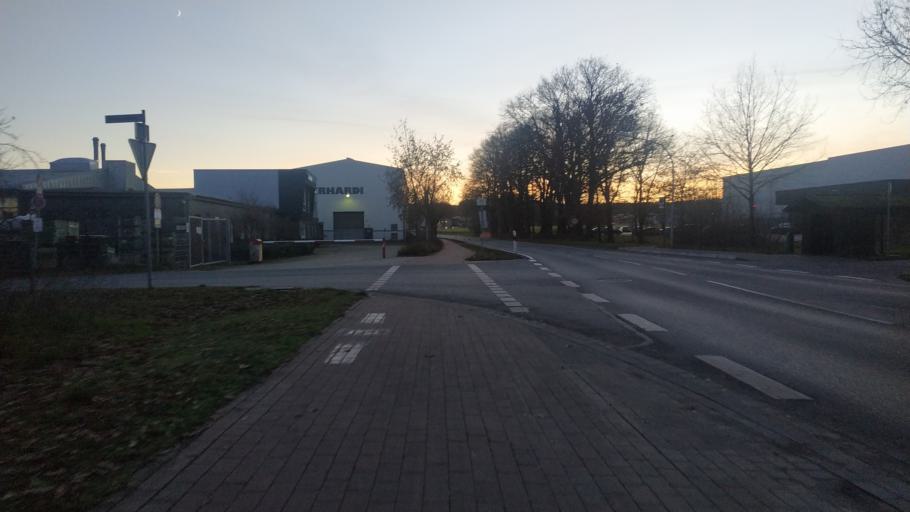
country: DE
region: North Rhine-Westphalia
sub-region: Regierungsbezirk Munster
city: Birgte
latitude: 52.2819
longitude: 7.6706
